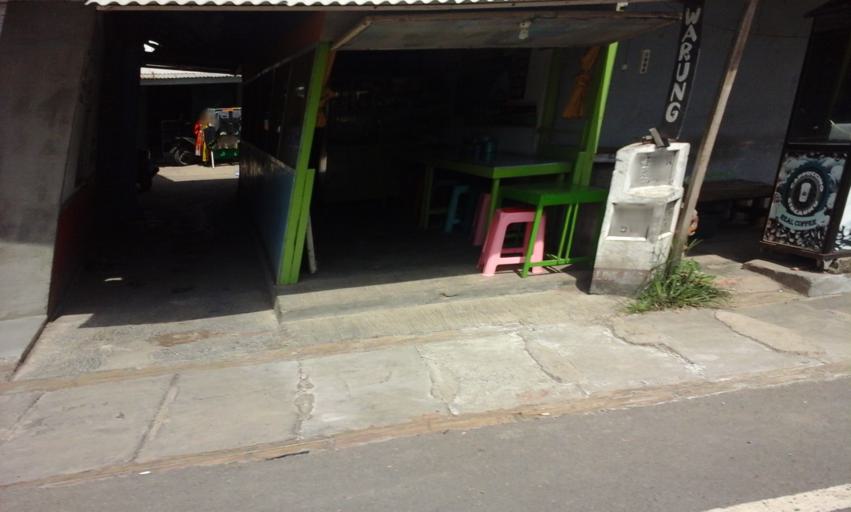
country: ID
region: East Java
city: Klatakan
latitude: -8.1237
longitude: 114.3971
